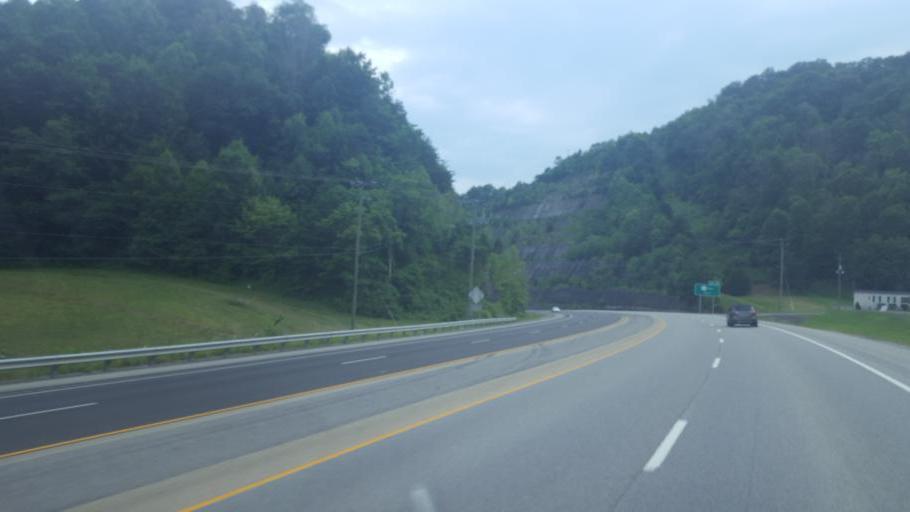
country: US
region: Kentucky
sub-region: Pike County
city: Pikeville
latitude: 37.4174
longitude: -82.5263
